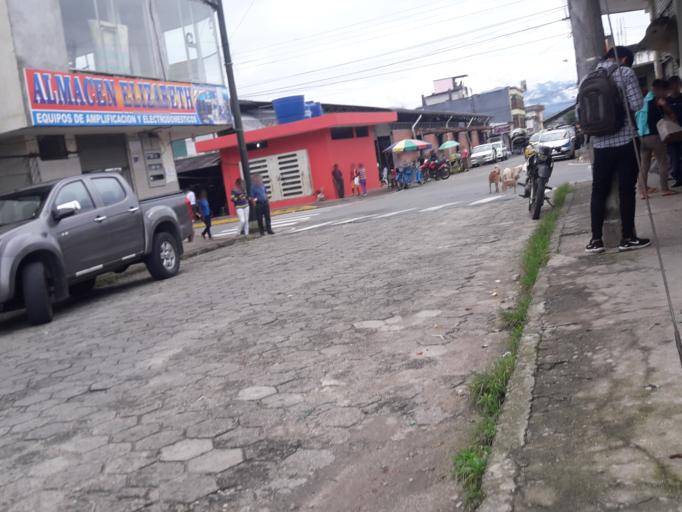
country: EC
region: Napo
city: Tena
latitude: -1.0016
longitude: -77.8121
